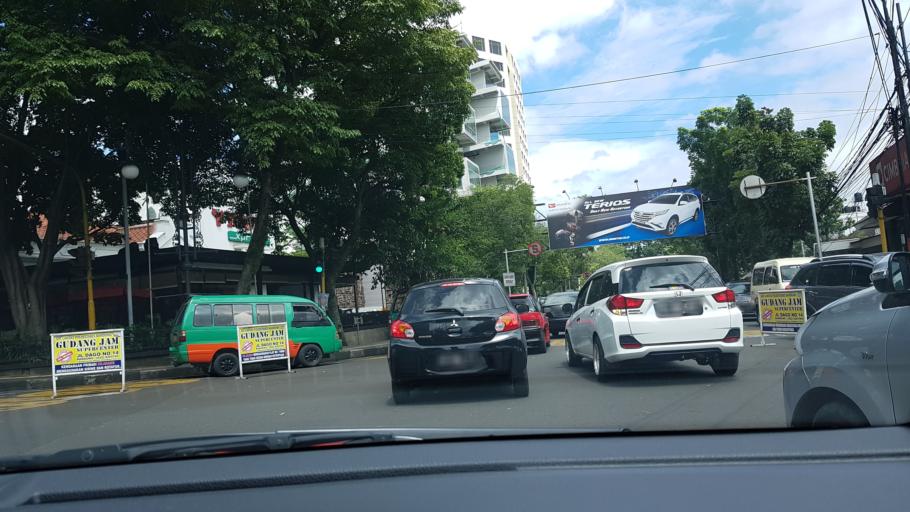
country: ID
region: West Java
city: Bandung
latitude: -6.9098
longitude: 107.6104
